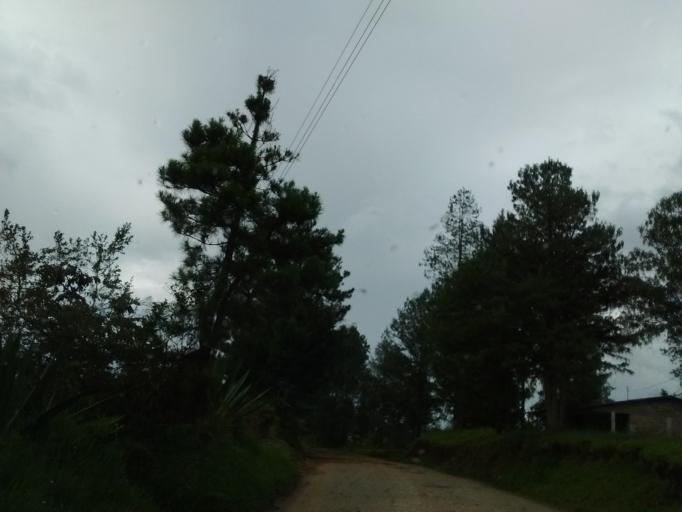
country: CO
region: Cauca
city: Cajibio
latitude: 2.5837
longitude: -76.6713
